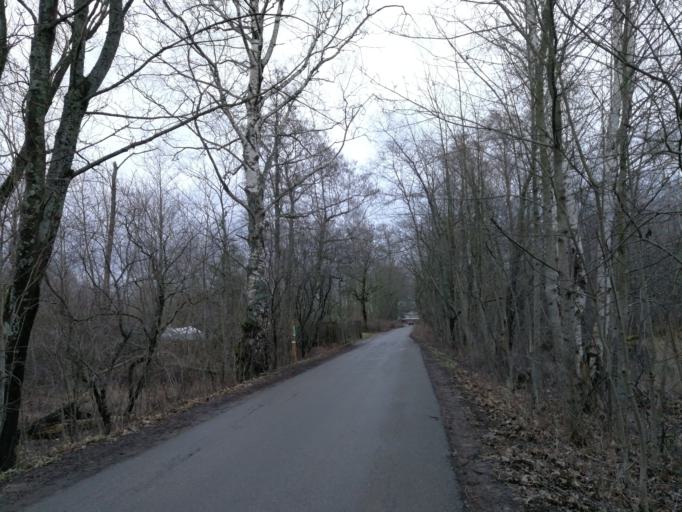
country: LV
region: Riga
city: Daugavgriva
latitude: 57.0609
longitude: 24.0463
